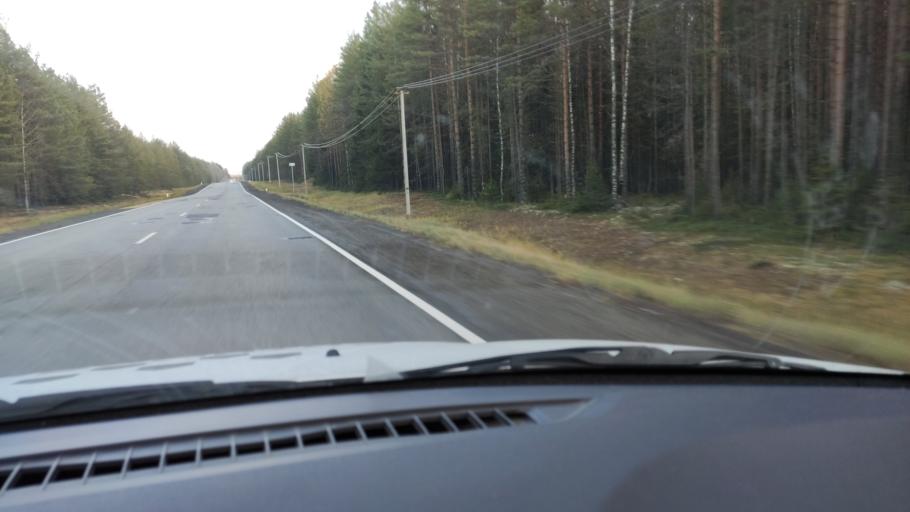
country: RU
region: Kirov
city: Belaya Kholunitsa
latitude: 58.9076
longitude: 51.0026
